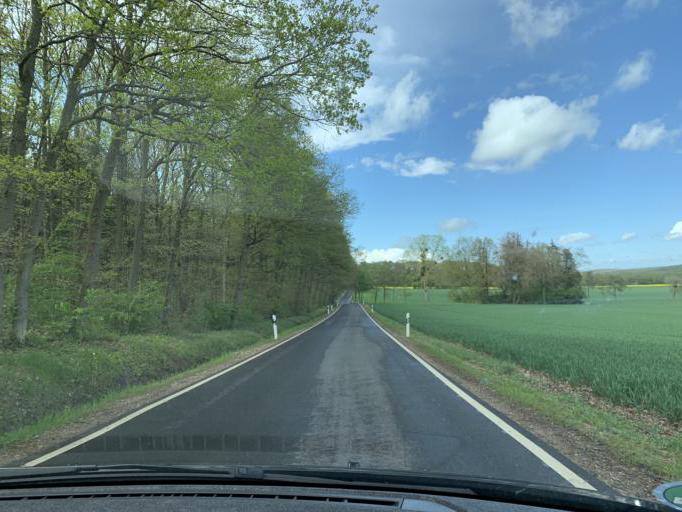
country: DE
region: North Rhine-Westphalia
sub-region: Regierungsbezirk Koln
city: Bad Munstereifel
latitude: 50.6002
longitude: 6.7348
